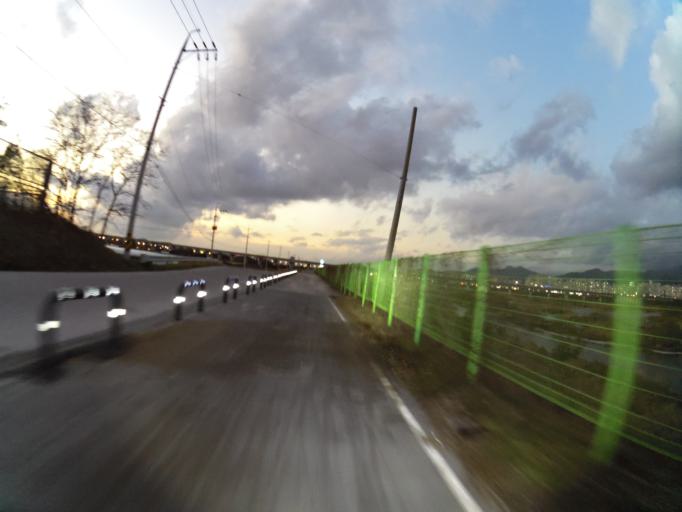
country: KR
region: Gyeongsangbuk-do
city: Gyeongsan-si
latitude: 35.8551
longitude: 128.7289
